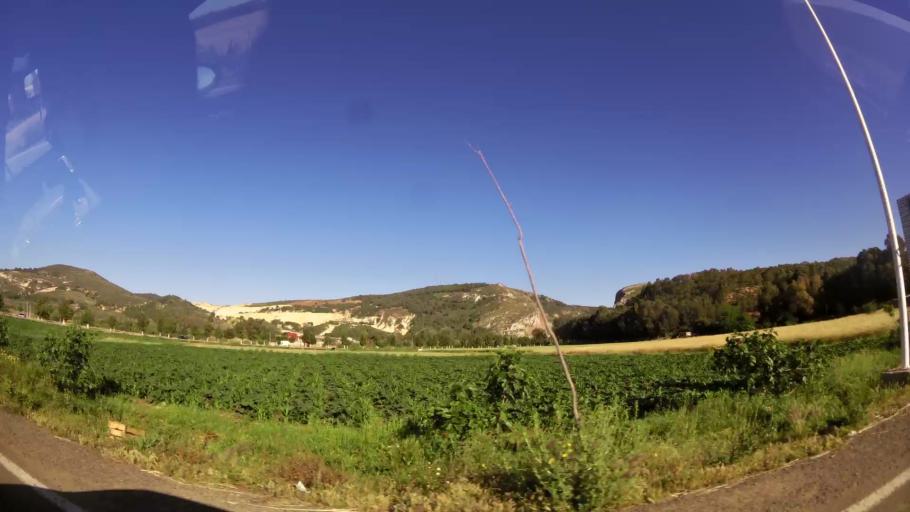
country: MA
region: Oriental
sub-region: Berkane-Taourirt
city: Madagh
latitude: 35.0658
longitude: -2.2176
